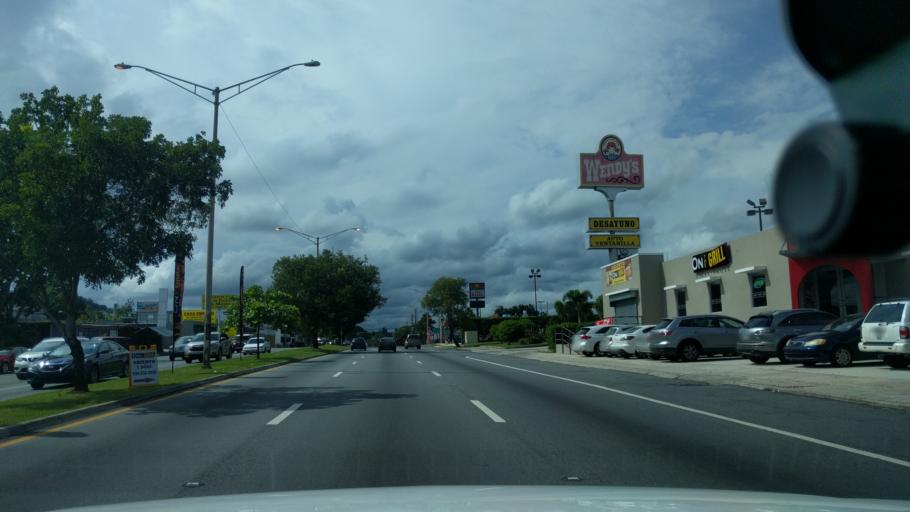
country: PR
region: Bayamon
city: Bayamon
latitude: 18.3655
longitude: -66.1735
